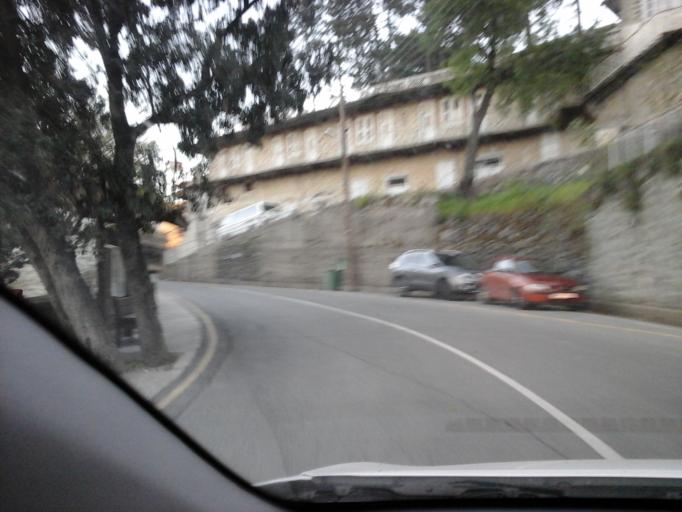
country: CY
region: Lefkosia
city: Kakopetria
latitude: 34.9688
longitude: 32.8271
